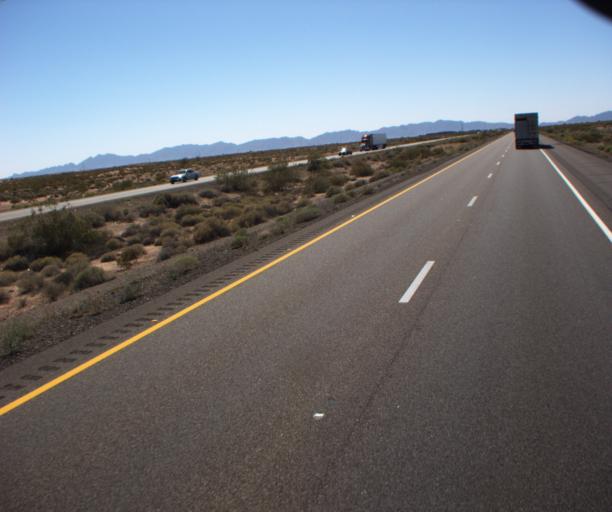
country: US
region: Arizona
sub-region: Yuma County
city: Wellton
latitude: 32.8122
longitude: -113.5108
